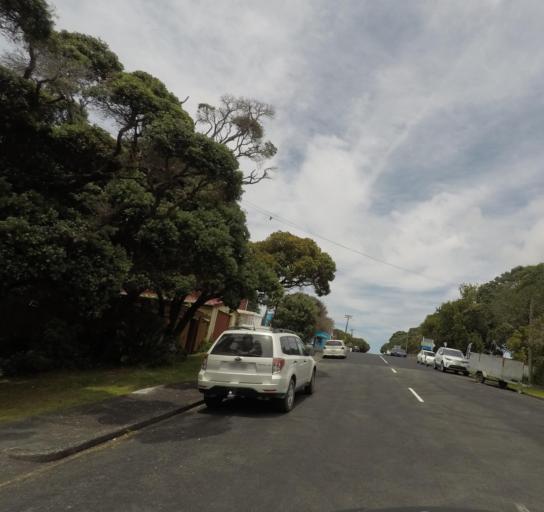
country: NZ
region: Auckland
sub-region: Auckland
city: Warkworth
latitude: -36.2898
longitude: 174.8048
